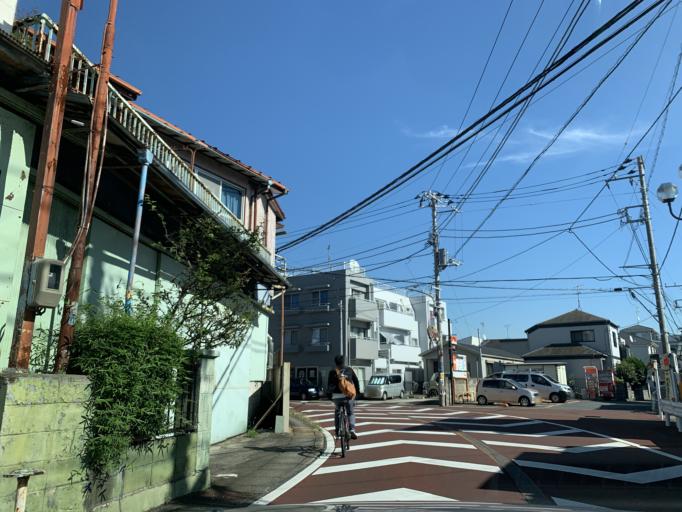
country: JP
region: Tokyo
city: Urayasu
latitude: 35.6902
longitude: 139.9151
